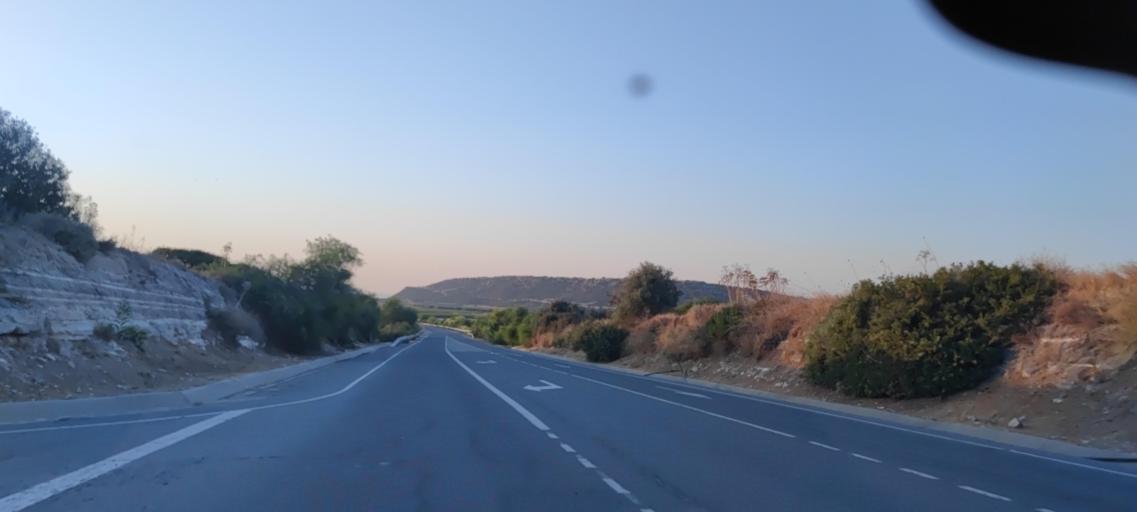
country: CY
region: Limassol
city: Pissouri
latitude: 34.6804
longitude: 32.7697
